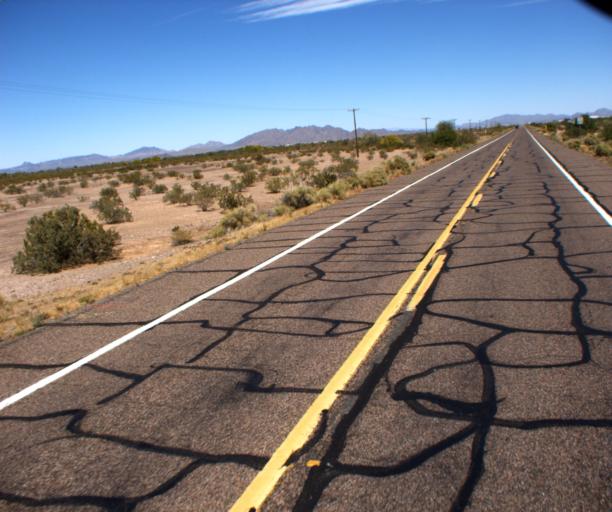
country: US
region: Arizona
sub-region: Maricopa County
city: Gila Bend
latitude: 32.9025
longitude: -112.7420
